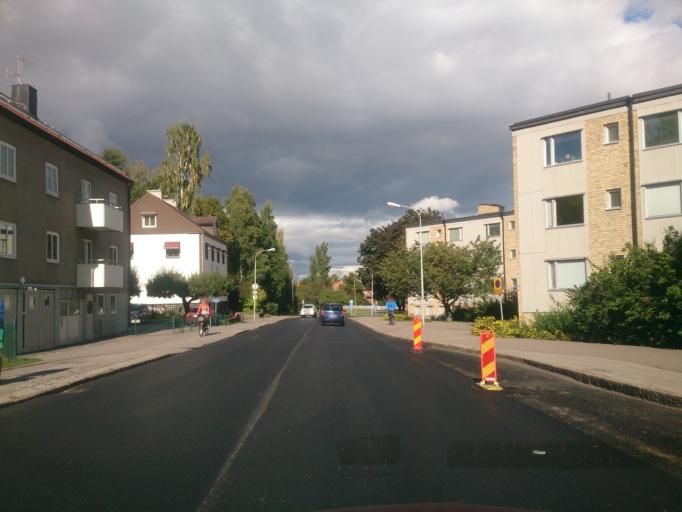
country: SE
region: OEstergoetland
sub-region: Linkopings Kommun
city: Linkoping
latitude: 58.3964
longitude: 15.6520
